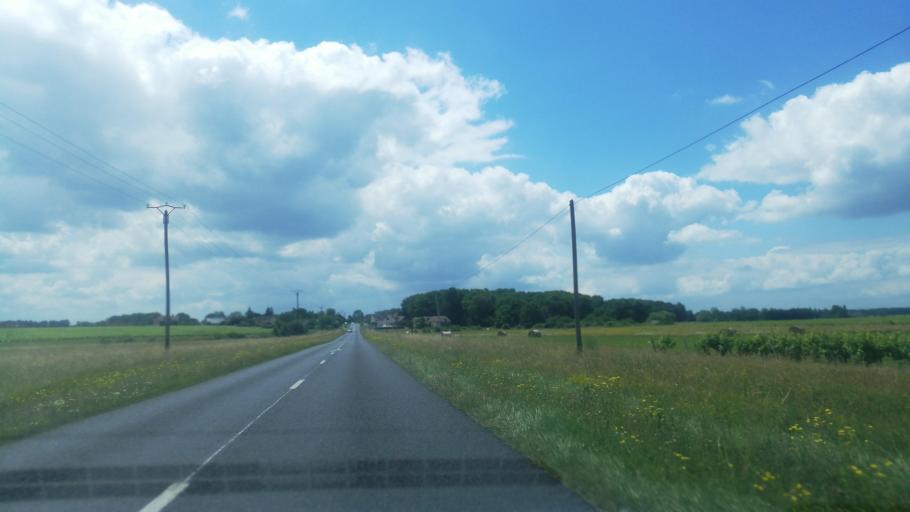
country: FR
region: Centre
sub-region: Departement du Loir-et-Cher
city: Contres
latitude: 47.3717
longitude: 1.4055
